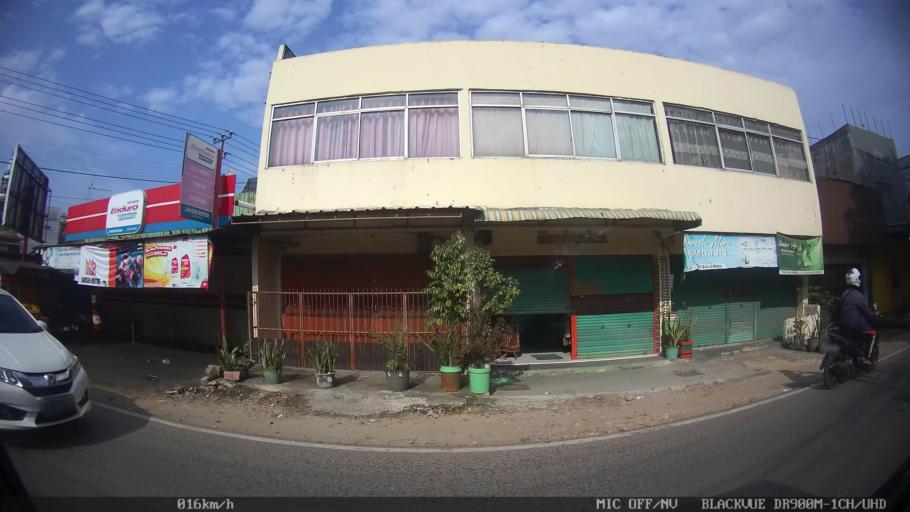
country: ID
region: Lampung
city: Panjang
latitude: -5.4749
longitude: 105.3218
